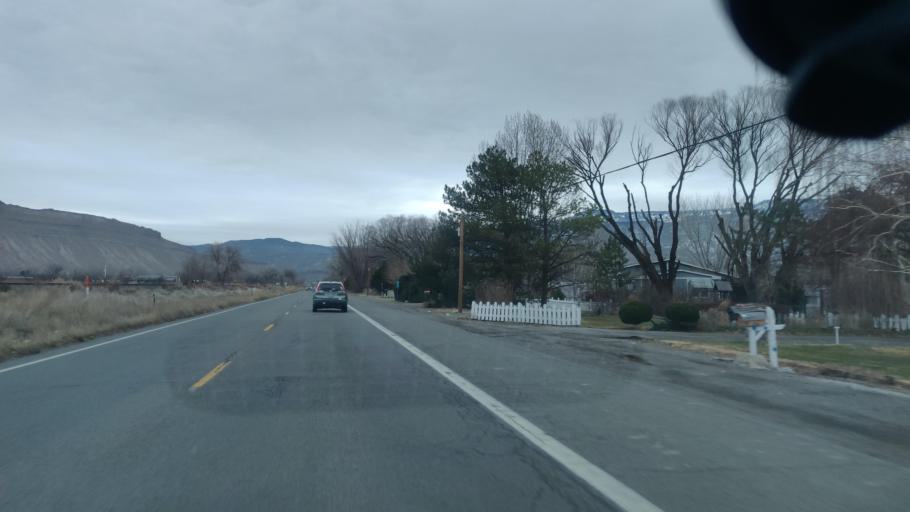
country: US
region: Colorado
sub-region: Mesa County
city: Palisade
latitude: 39.1013
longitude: -108.3925
